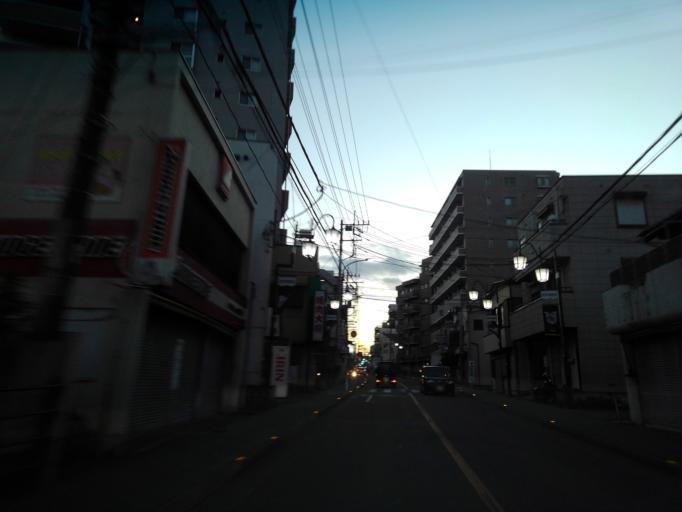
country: JP
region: Saitama
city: Tokorozawa
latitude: 35.7901
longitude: 139.4589
